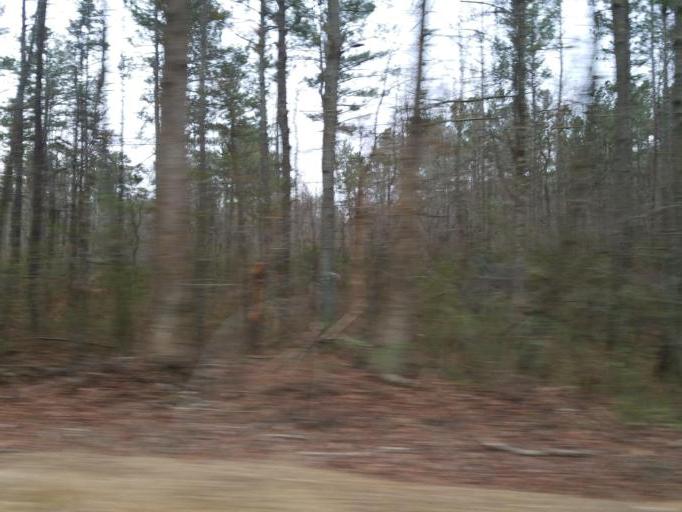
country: US
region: Georgia
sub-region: Dawson County
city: Dawsonville
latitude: 34.4511
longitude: -84.1231
